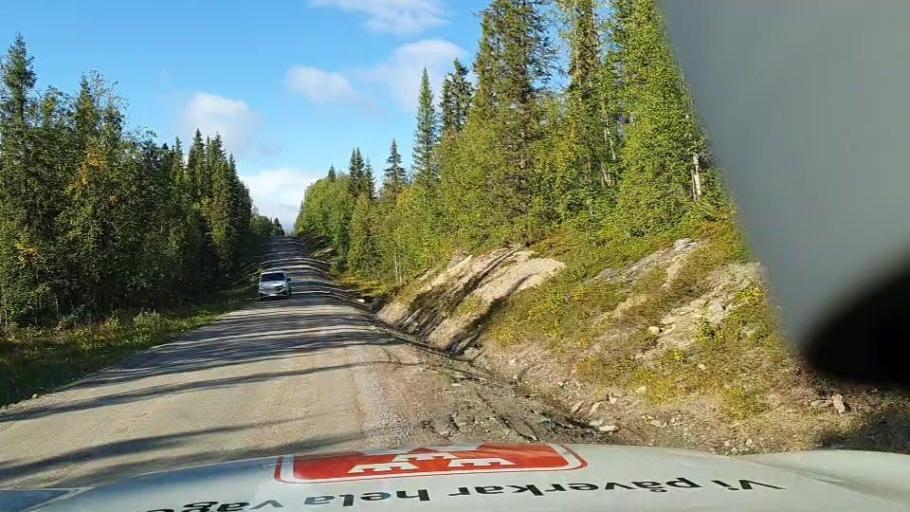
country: SE
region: Jaemtland
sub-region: Stroemsunds Kommun
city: Stroemsund
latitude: 64.5601
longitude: 15.0945
